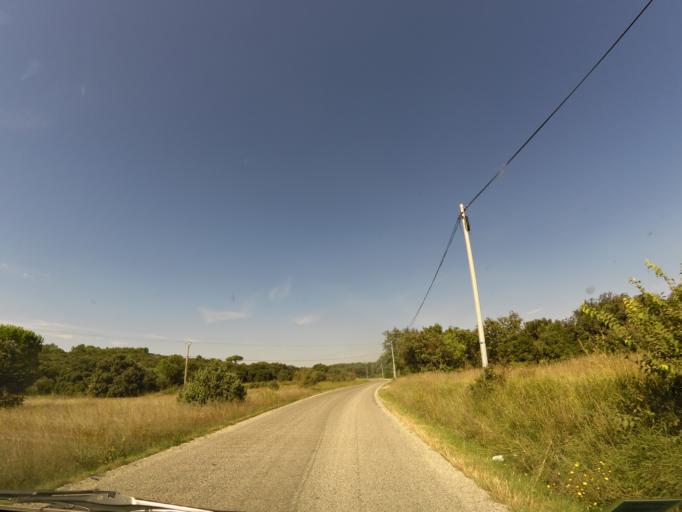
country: FR
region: Languedoc-Roussillon
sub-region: Departement du Gard
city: Uchaud
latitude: 43.7632
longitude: 4.2547
